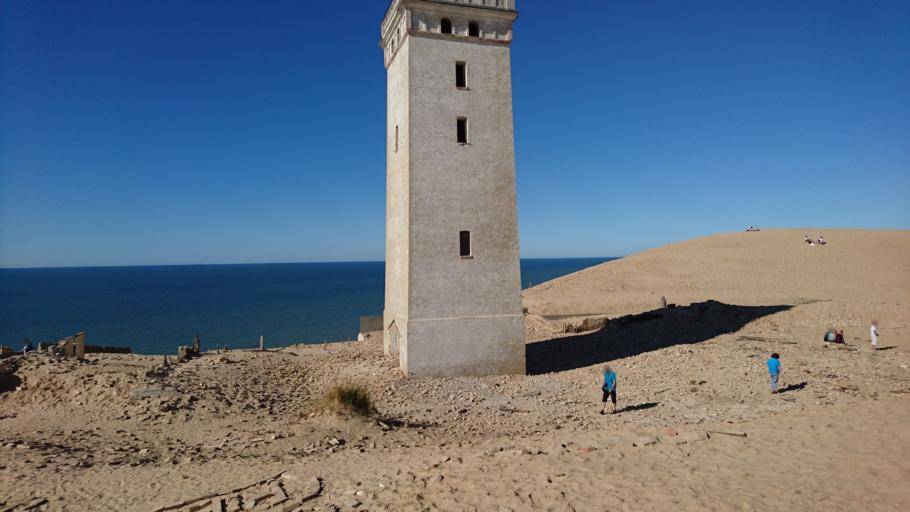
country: DK
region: North Denmark
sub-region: Hjorring Kommune
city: Vra
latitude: 57.4486
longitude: 9.7743
